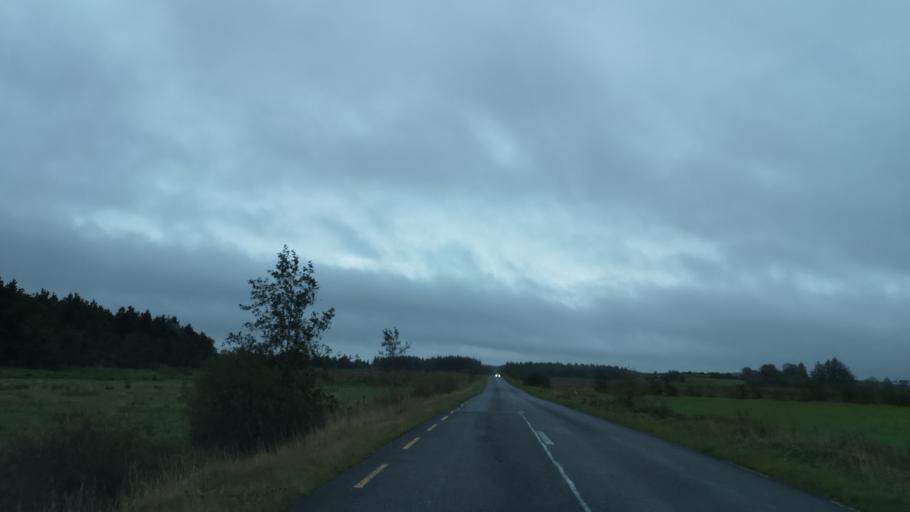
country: IE
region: Connaught
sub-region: Roscommon
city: Ballaghaderreen
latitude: 53.8136
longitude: -8.6539
